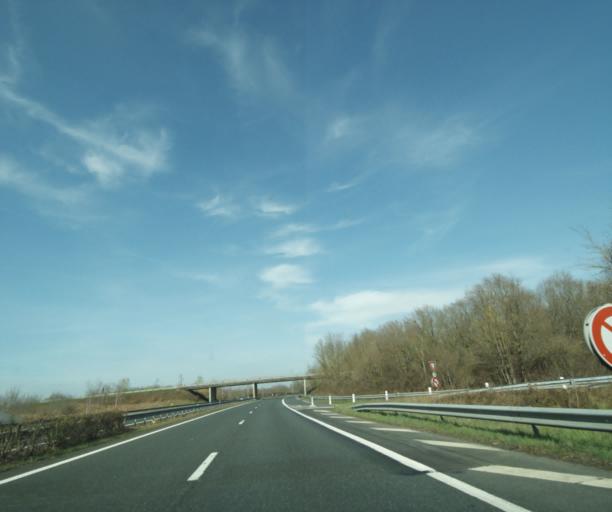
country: FR
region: Centre
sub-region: Departement de l'Indre
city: Luant
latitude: 46.6982
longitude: 1.5836
